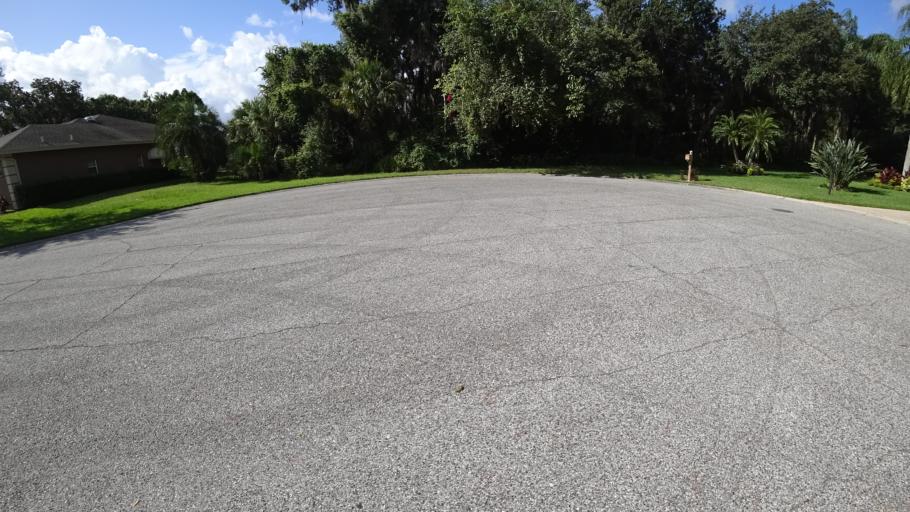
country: US
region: Florida
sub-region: Sarasota County
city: Desoto Lakes
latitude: 27.3958
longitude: -82.4840
